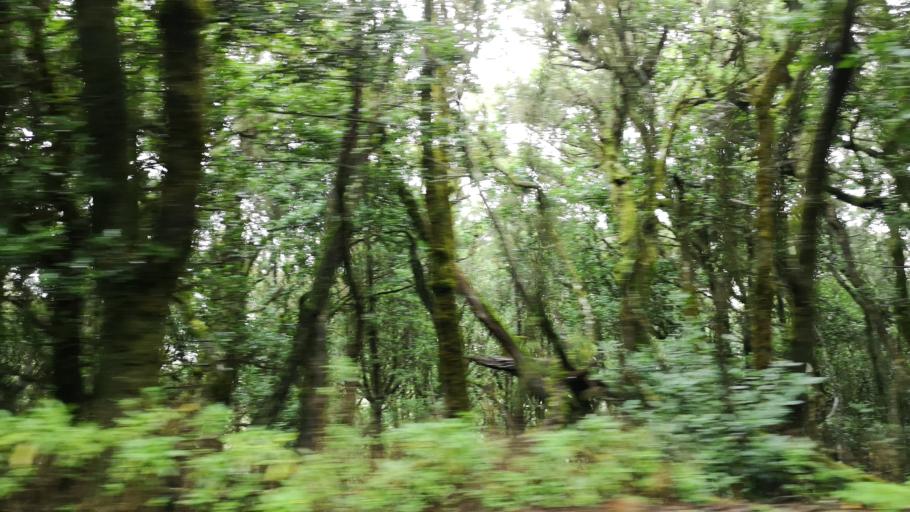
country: ES
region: Canary Islands
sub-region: Provincia de Santa Cruz de Tenerife
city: Vallehermosa
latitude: 28.1531
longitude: -17.3039
